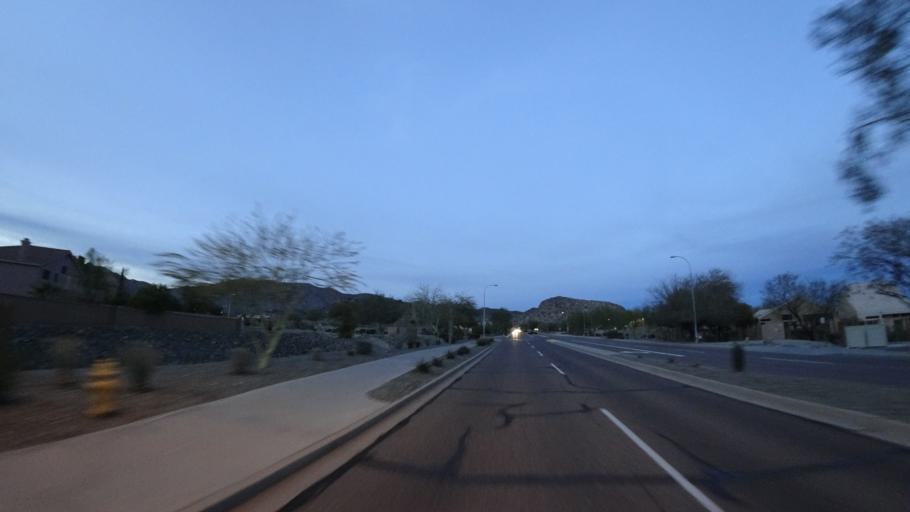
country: US
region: Arizona
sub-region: Maricopa County
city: Guadalupe
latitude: 33.3018
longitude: -112.0585
